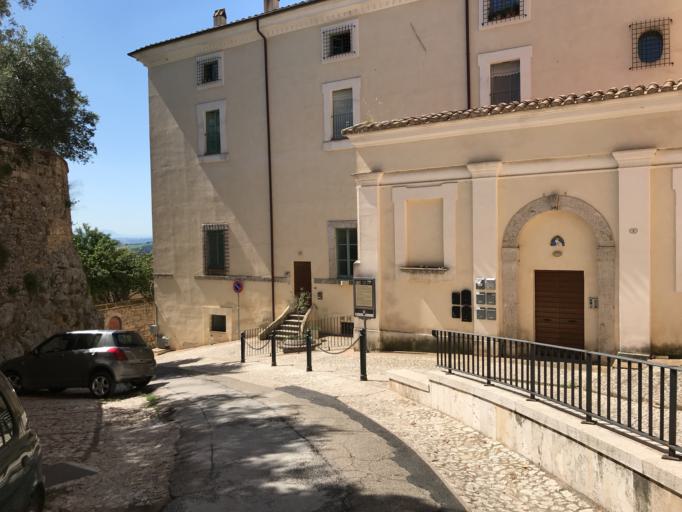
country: IT
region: Umbria
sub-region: Provincia di Terni
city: Amelia
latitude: 42.5581
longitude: 12.4108
